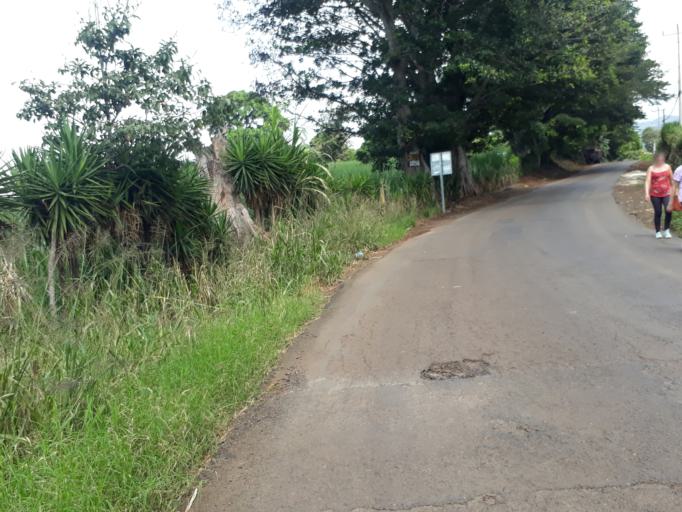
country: CR
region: Alajuela
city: Carrillos
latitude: 10.0227
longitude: -84.3364
